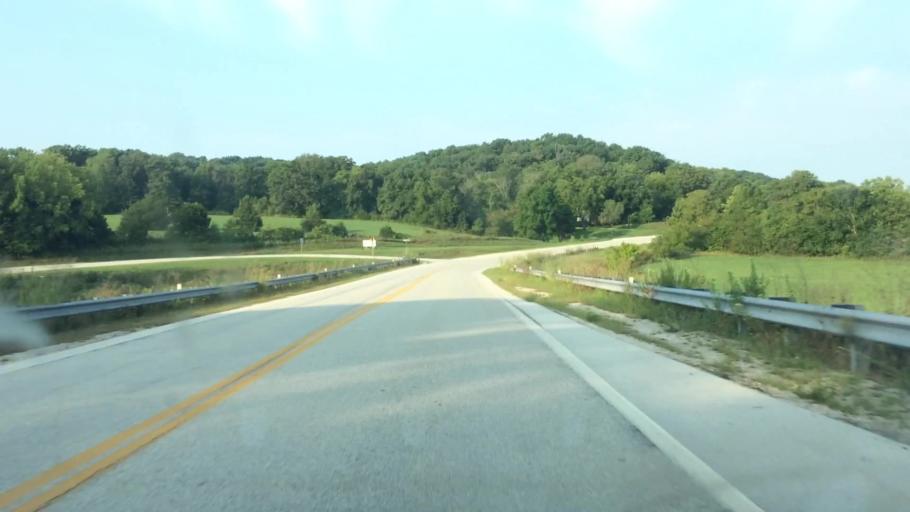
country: US
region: Missouri
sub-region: Greene County
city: Strafford
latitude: 37.1918
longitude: -93.1052
